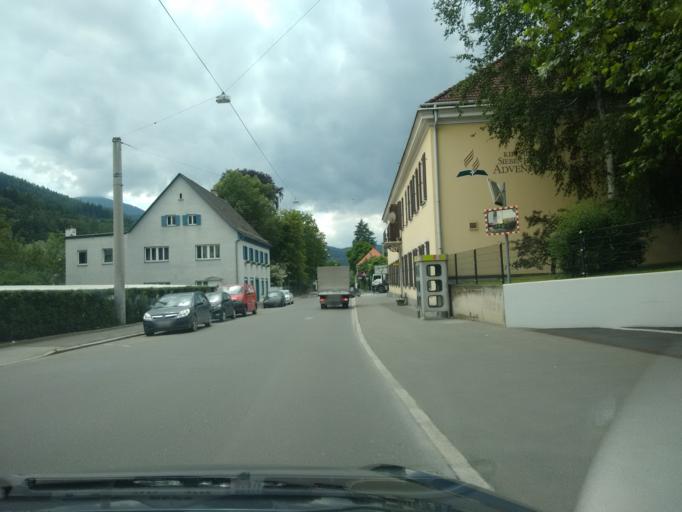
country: AT
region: Styria
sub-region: Politischer Bezirk Bruck-Muerzzuschlag
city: Bruck an der Mur
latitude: 47.4079
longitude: 15.2645
